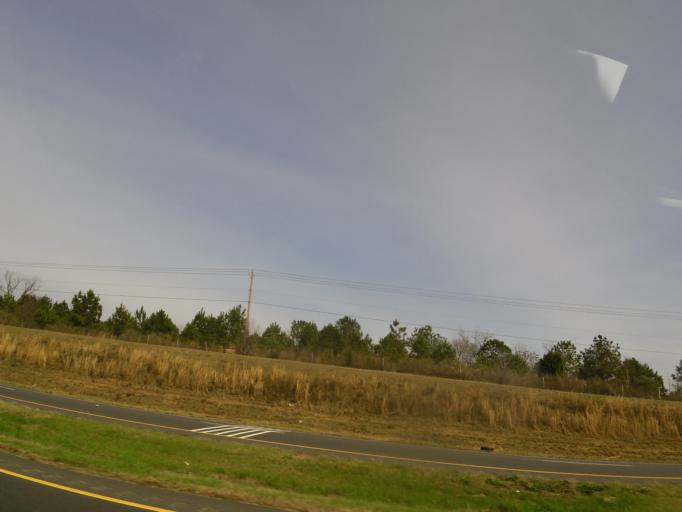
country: US
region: Alabama
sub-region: Dale County
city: Midland City
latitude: 31.2850
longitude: -85.4660
